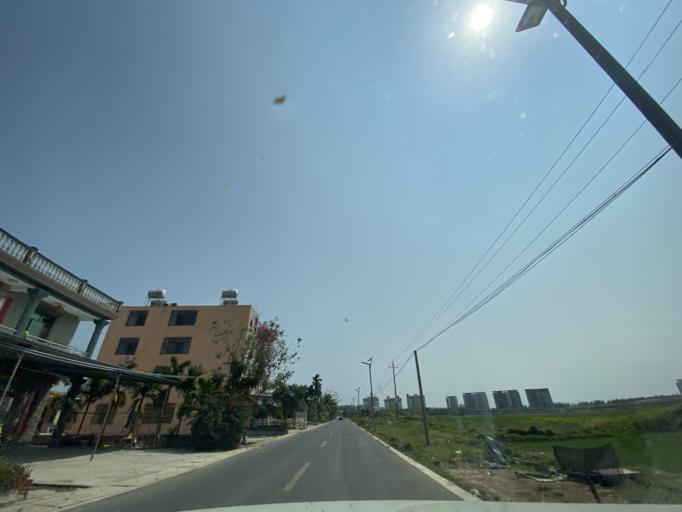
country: CN
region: Hainan
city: Yingzhou
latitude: 18.4110
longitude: 109.8152
